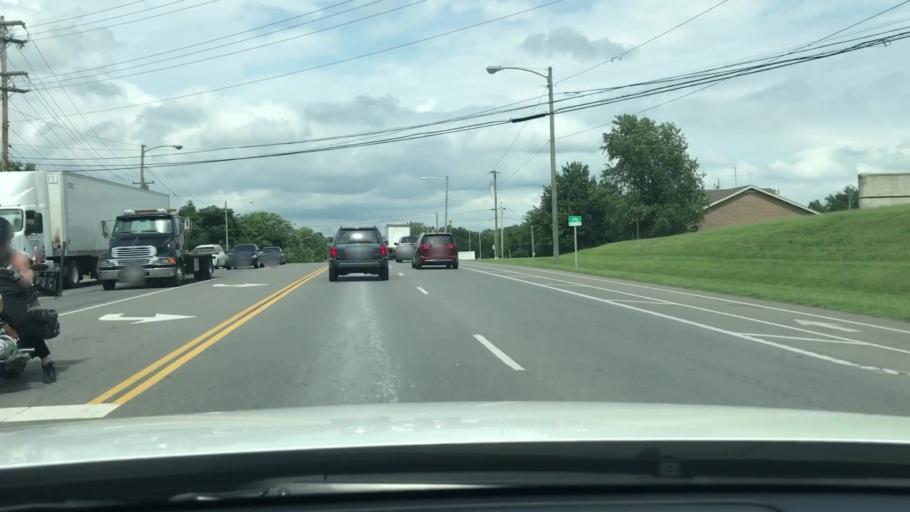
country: US
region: Tennessee
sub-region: Davidson County
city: Oak Hill
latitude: 36.0897
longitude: -86.6883
